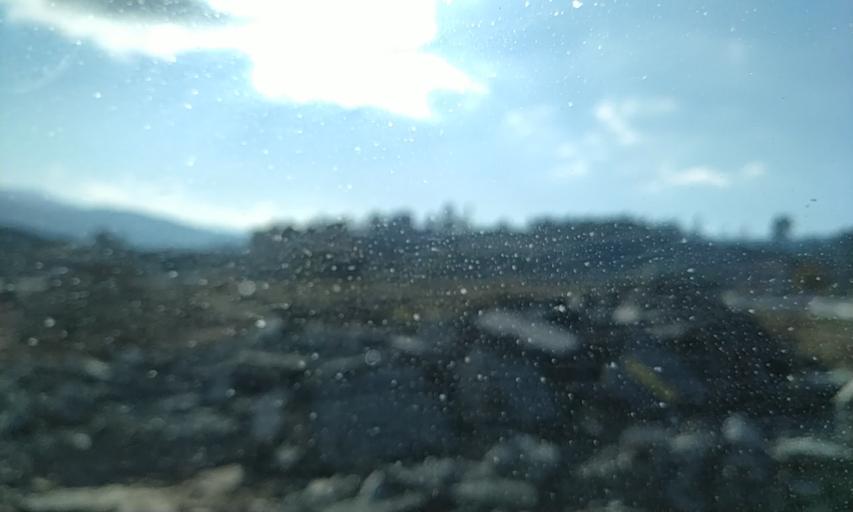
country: PT
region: Braga
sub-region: Celorico de Basto
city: Celorico de Basto
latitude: 41.3994
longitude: -7.9867
